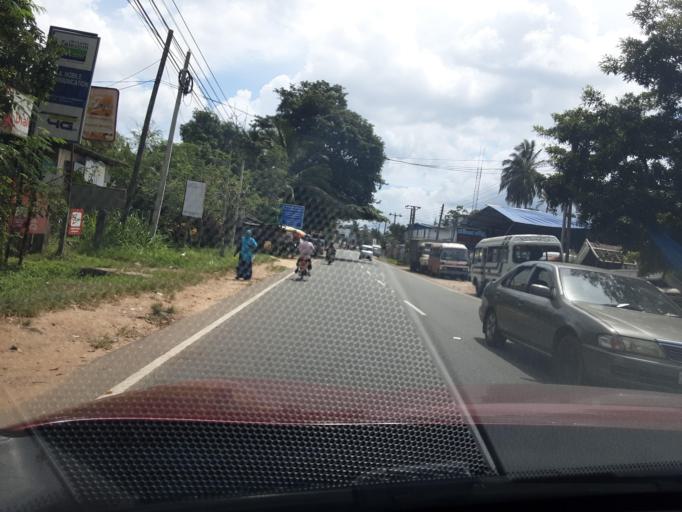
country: LK
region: North Western
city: Kuliyapitiya
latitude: 7.4511
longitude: 80.1889
